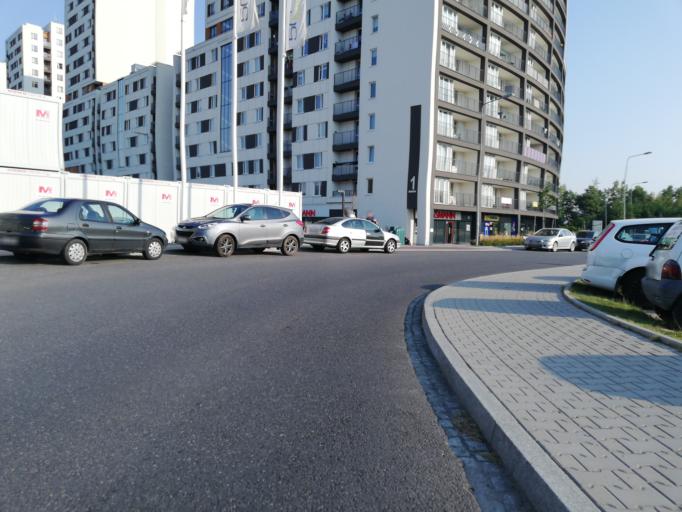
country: PL
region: Lesser Poland Voivodeship
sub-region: Krakow
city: Krakow
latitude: 50.0823
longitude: 19.9995
